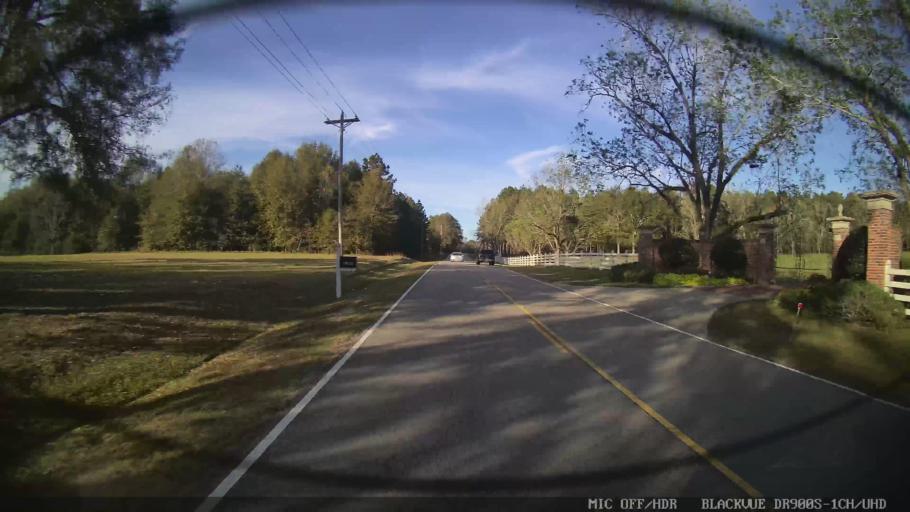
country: US
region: Mississippi
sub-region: Lamar County
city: Purvis
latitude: 31.1815
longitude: -89.2921
